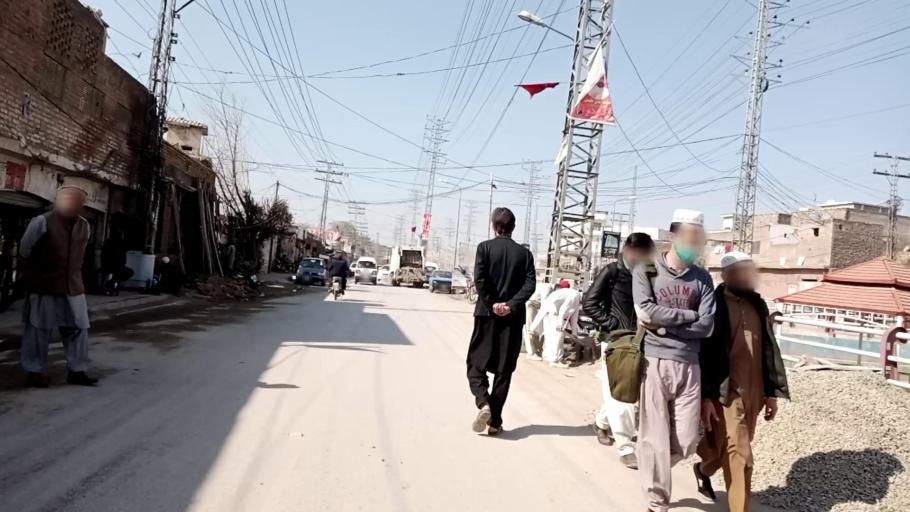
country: PK
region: Khyber Pakhtunkhwa
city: Peshawar
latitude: 33.9933
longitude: 71.4765
